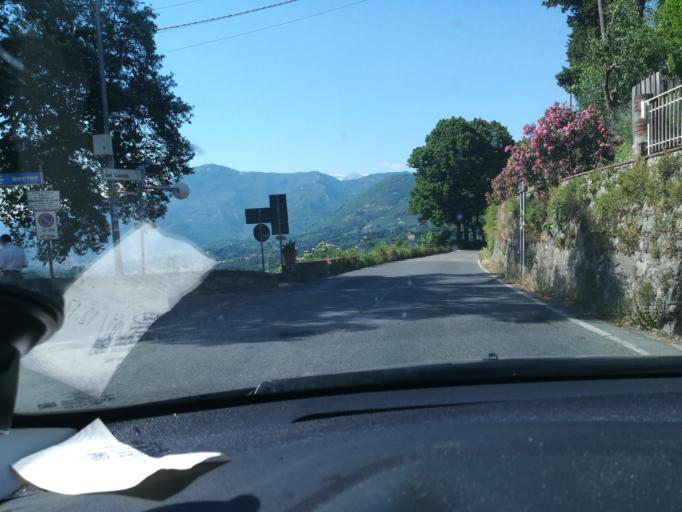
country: IT
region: Tuscany
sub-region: Provincia di Lucca
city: Stiava
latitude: 43.9108
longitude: 10.3387
